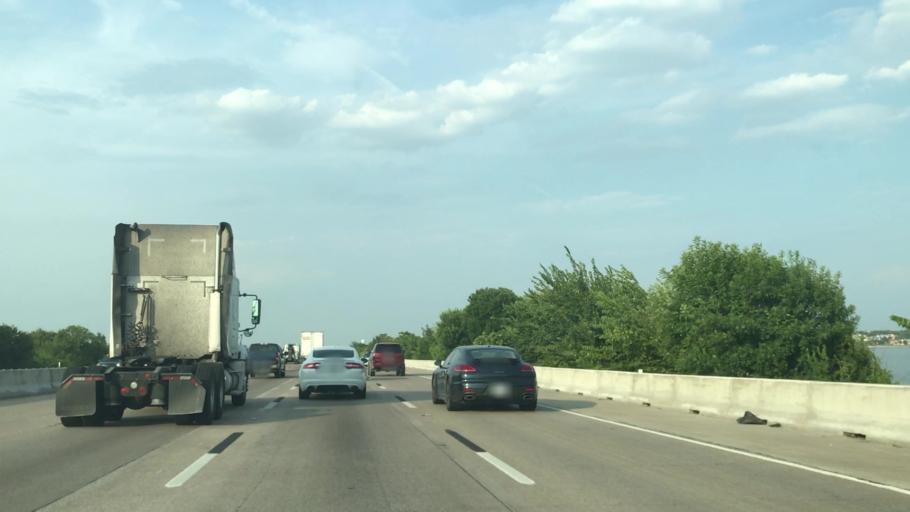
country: US
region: Texas
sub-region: Rockwall County
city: Heath
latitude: 32.8804
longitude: -96.5085
